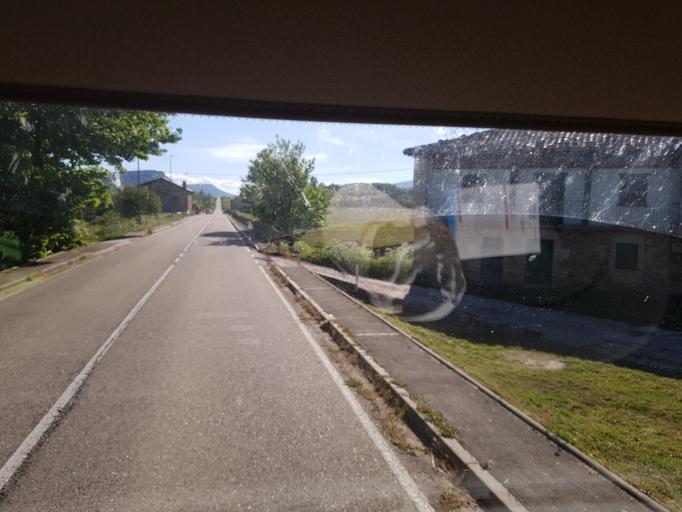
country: ES
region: Castille and Leon
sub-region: Provincia de Burgos
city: Espinosa de los Monteros
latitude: 43.0617
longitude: -3.5893
